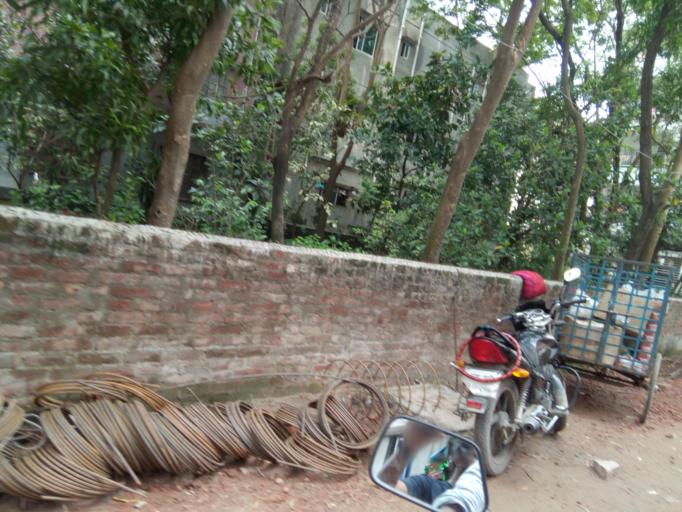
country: BD
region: Dhaka
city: Paltan
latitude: 23.7530
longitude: 90.4373
